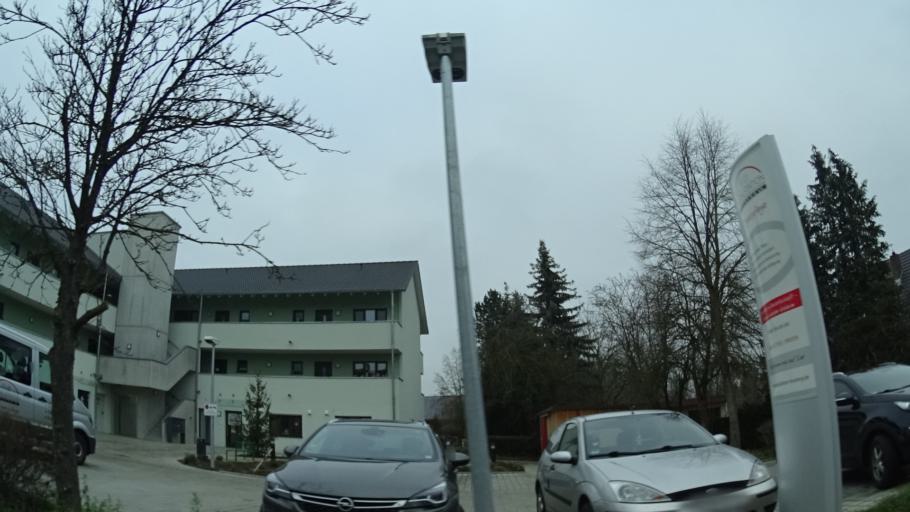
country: DE
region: Baden-Wuerttemberg
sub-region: Regierungsbezirk Stuttgart
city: Boxberg
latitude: 49.4802
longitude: 9.6371
